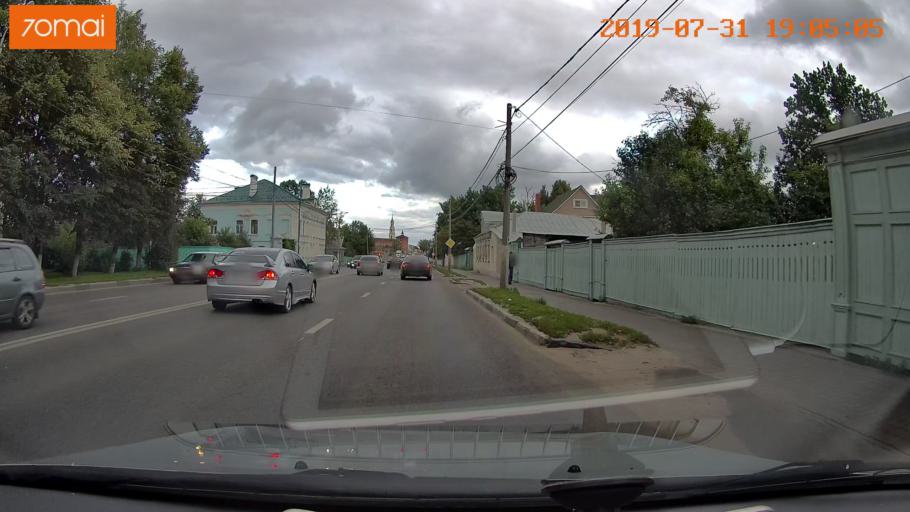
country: RU
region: Moskovskaya
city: Raduzhnyy
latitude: 55.1068
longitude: 38.7447
